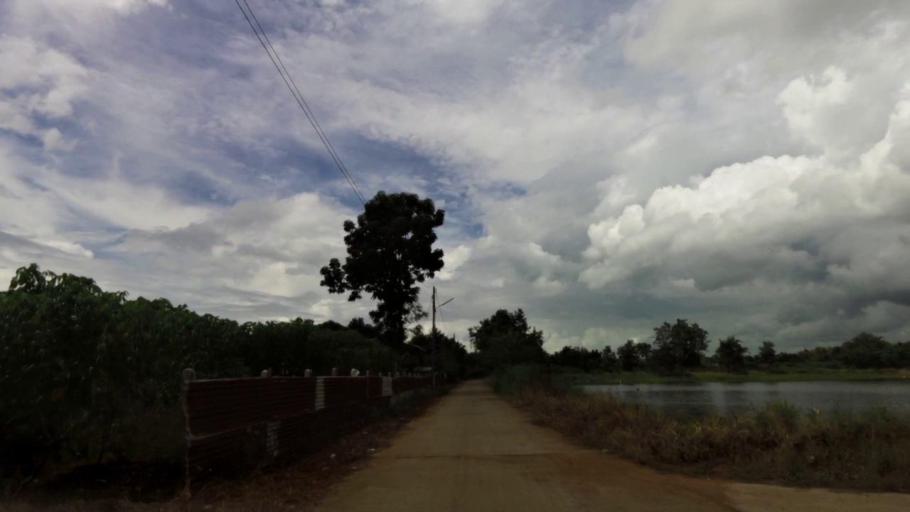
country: TH
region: Nakhon Sawan
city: Phai Sali
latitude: 15.6064
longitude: 100.6552
